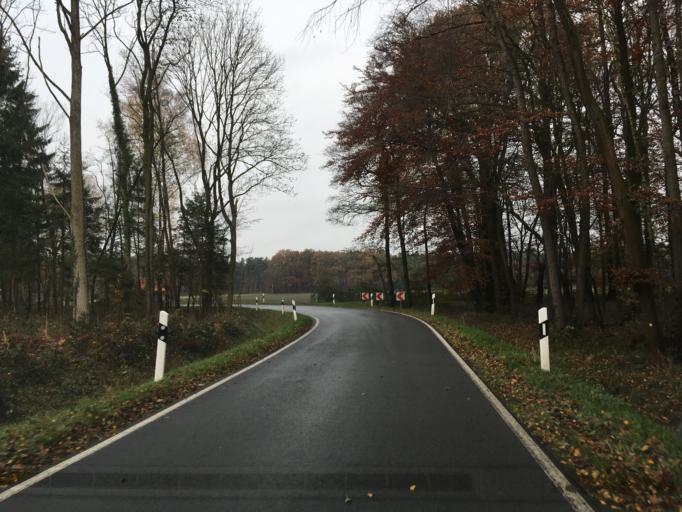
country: DE
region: North Rhine-Westphalia
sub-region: Regierungsbezirk Munster
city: Ahaus
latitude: 52.0189
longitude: 6.9966
